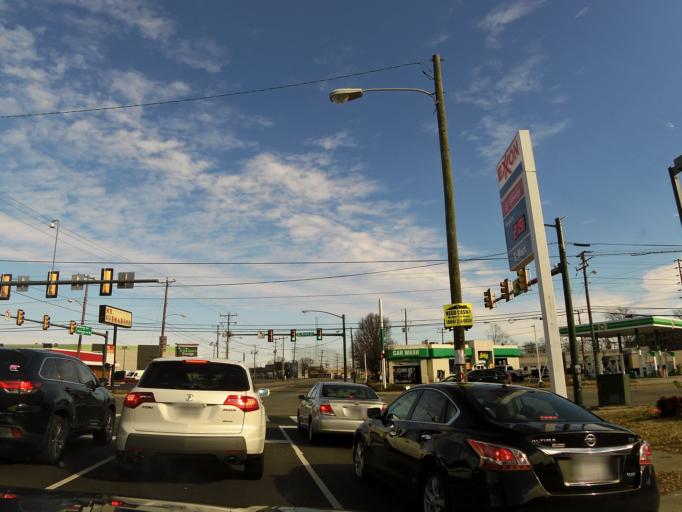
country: US
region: Virginia
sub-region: City of Richmond
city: Richmond
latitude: 37.5732
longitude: -77.4838
